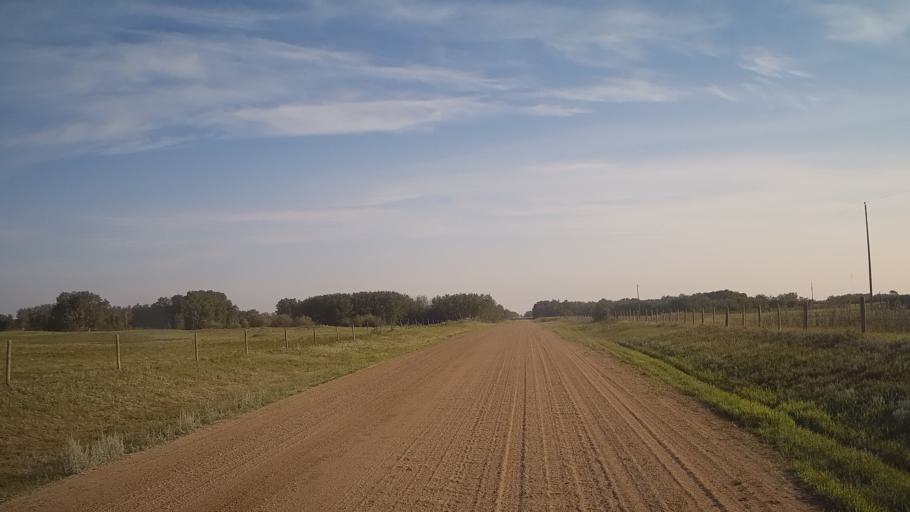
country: CA
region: Saskatchewan
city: Saskatoon
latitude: 51.8267
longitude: -106.5239
